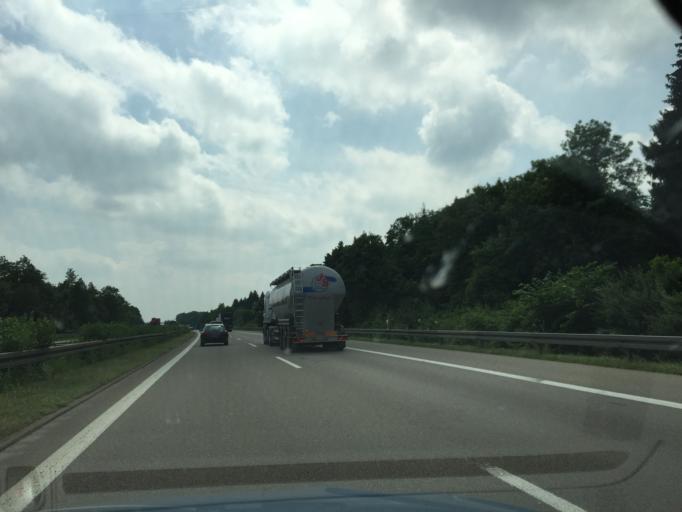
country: DE
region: Bavaria
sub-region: Swabia
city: Nersingen
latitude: 48.4253
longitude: 10.0977
